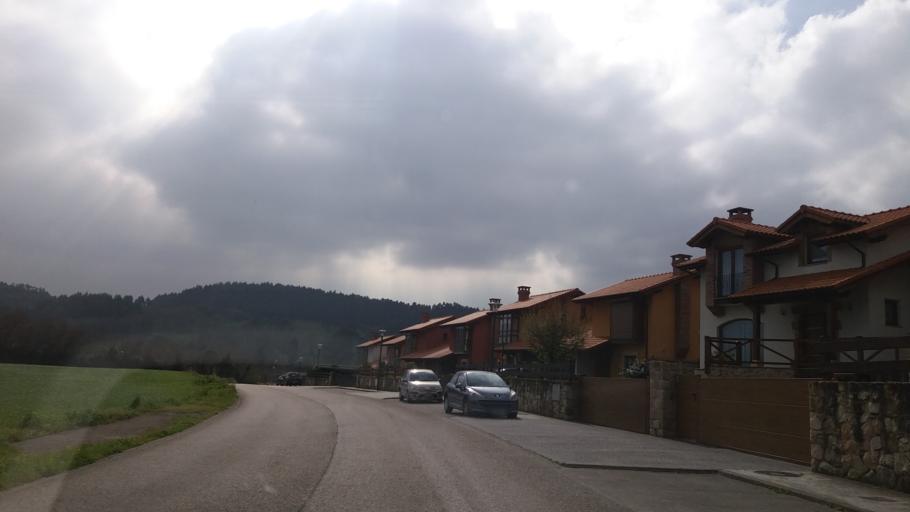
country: ES
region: Cantabria
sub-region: Provincia de Cantabria
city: Reocin
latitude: 43.3699
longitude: -4.0806
